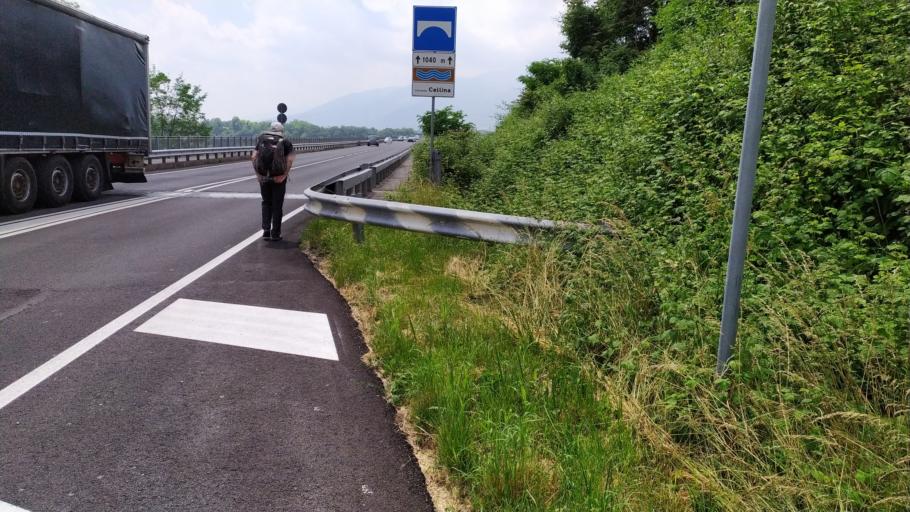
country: IT
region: Friuli Venezia Giulia
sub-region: Provincia di Pordenone
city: Vajont
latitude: 46.1520
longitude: 12.6838
